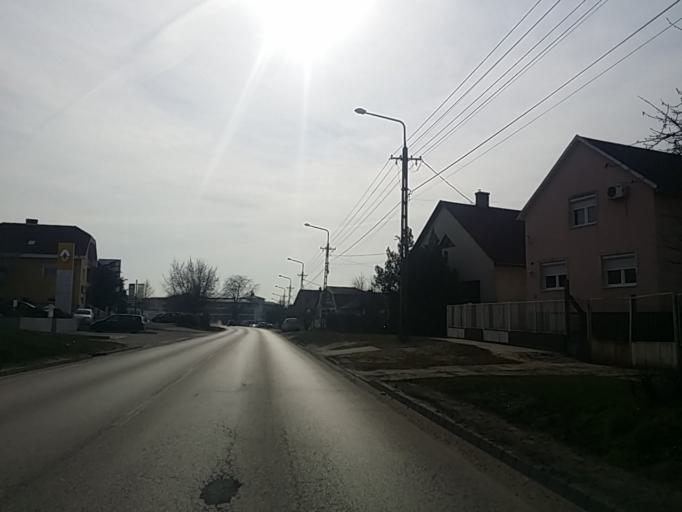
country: HU
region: Pest
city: Fot
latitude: 47.6210
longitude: 19.1892
